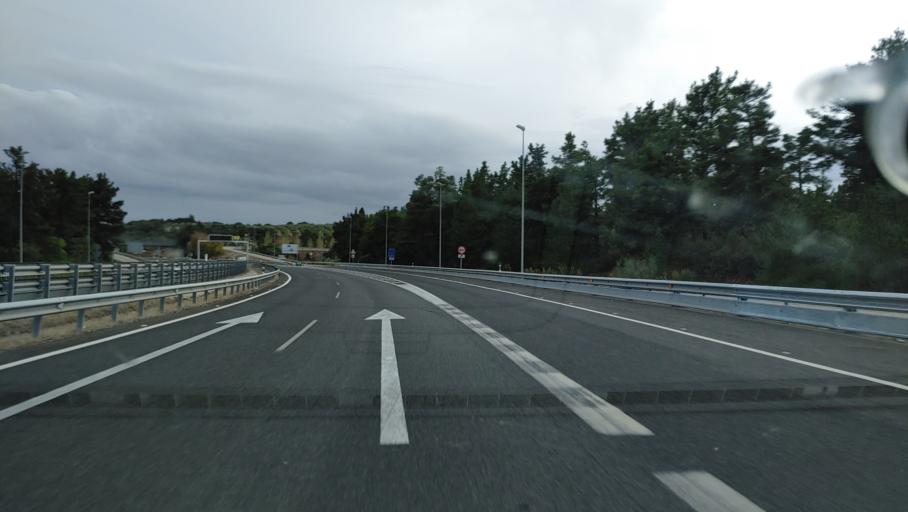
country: ES
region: Andalusia
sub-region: Provincia de Jaen
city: Santa Elena
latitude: 38.3411
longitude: -3.5452
